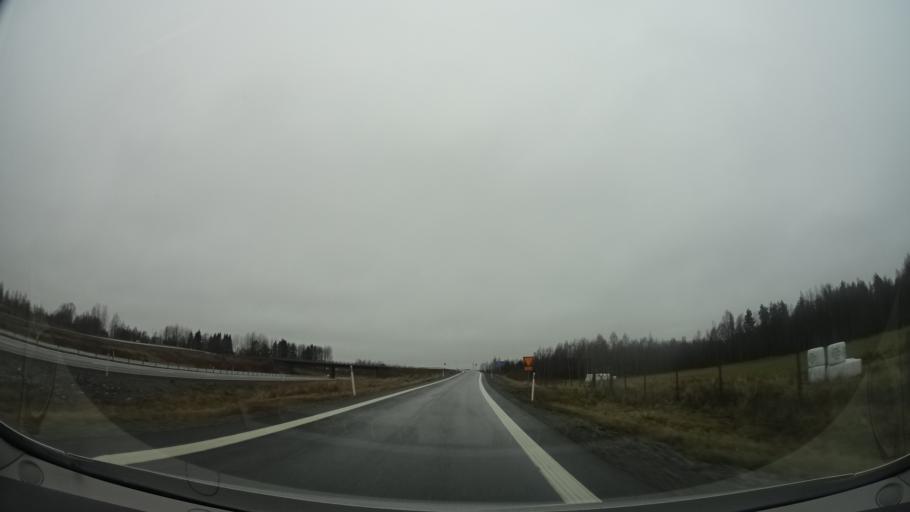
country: SE
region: Vaesterbotten
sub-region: Skelleftea Kommun
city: Kage
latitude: 64.8375
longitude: 20.9962
